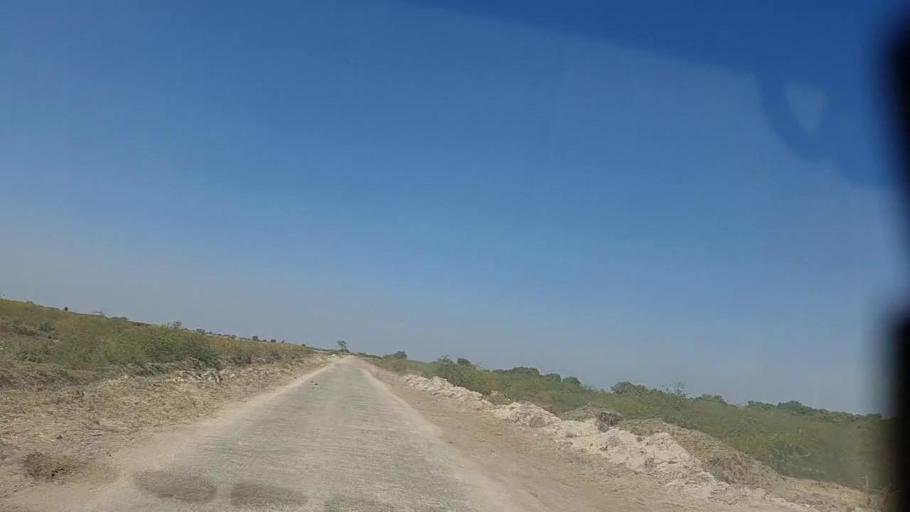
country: PK
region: Sindh
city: Mirwah Gorchani
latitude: 25.2233
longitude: 69.0225
